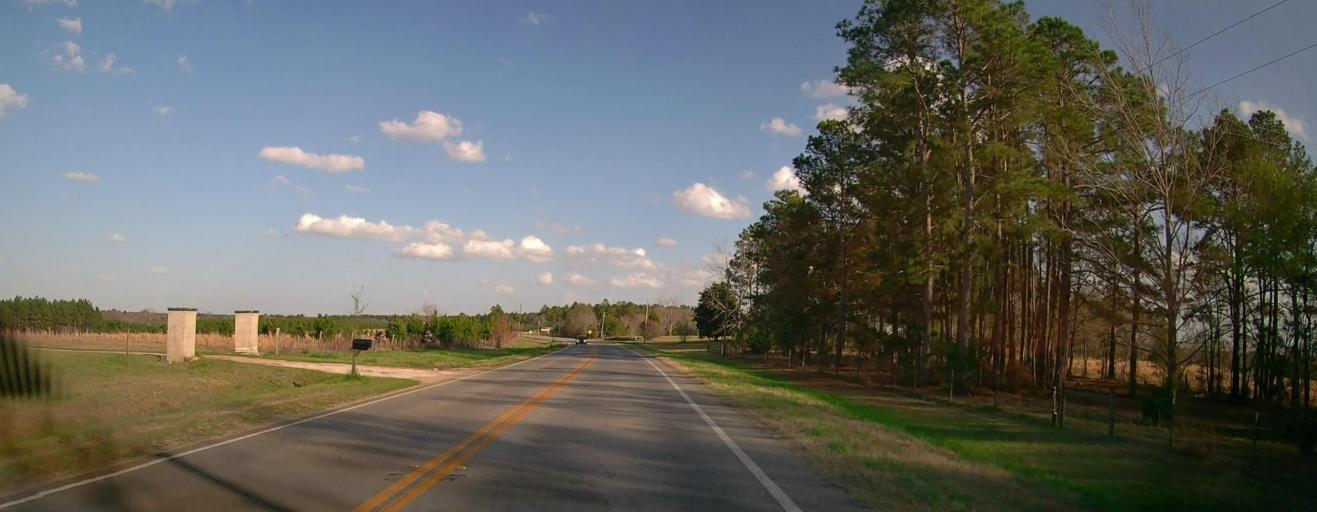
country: US
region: Georgia
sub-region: Toombs County
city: Lyons
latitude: 32.1761
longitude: -82.2846
